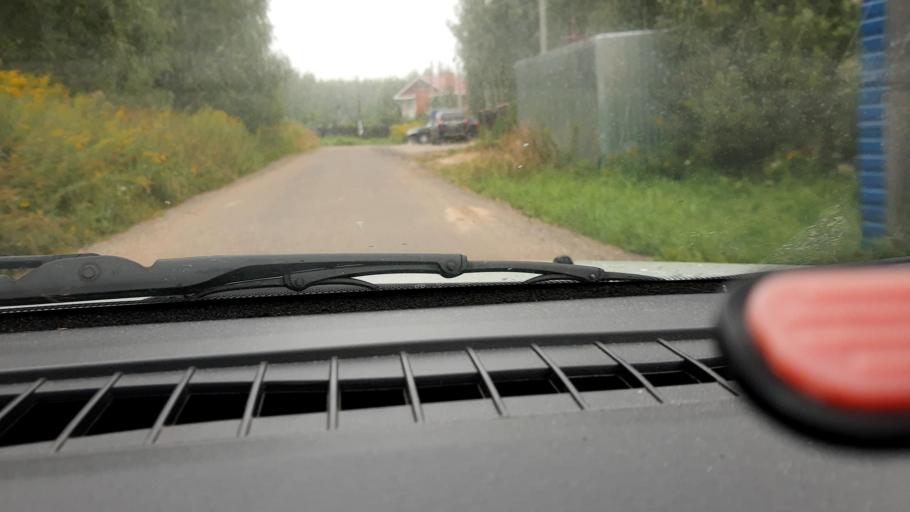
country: RU
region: Nizjnij Novgorod
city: Afonino
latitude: 56.2447
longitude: 44.0744
